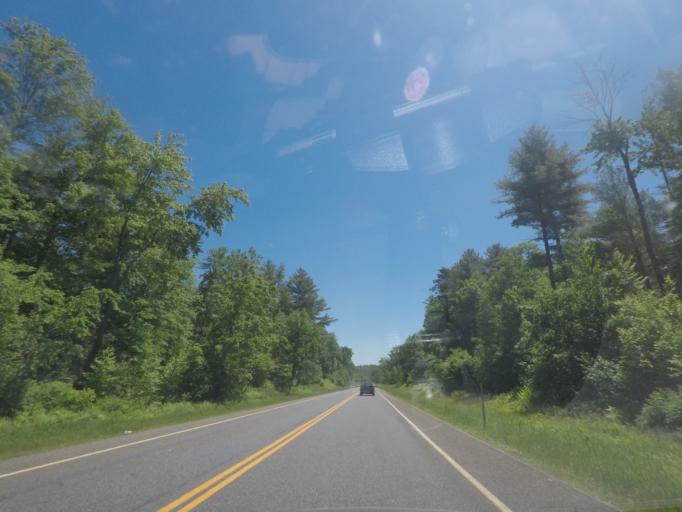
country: US
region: New York
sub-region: Saratoga County
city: Mechanicville
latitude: 42.9463
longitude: -73.7354
